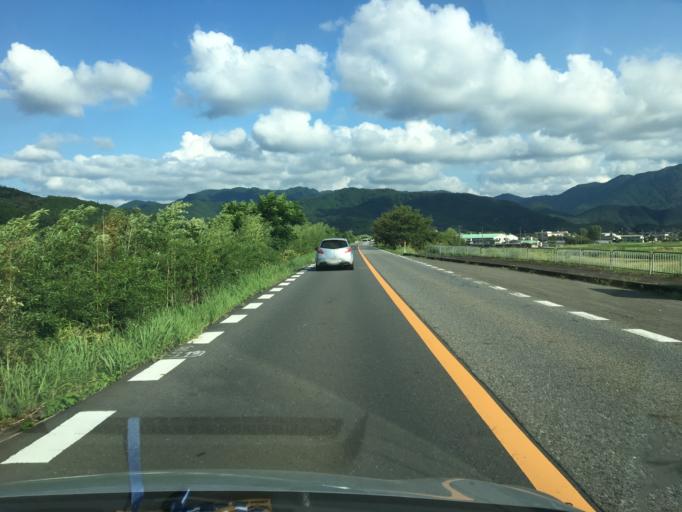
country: JP
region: Hyogo
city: Toyooka
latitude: 35.4412
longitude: 134.7830
